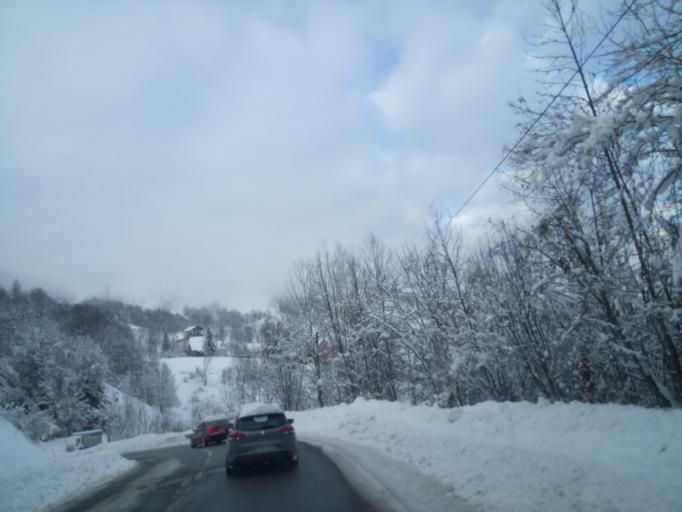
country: FR
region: Rhone-Alpes
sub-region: Departement de la Savoie
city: Saint-Jean-de-Maurienne
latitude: 45.2431
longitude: 6.2786
